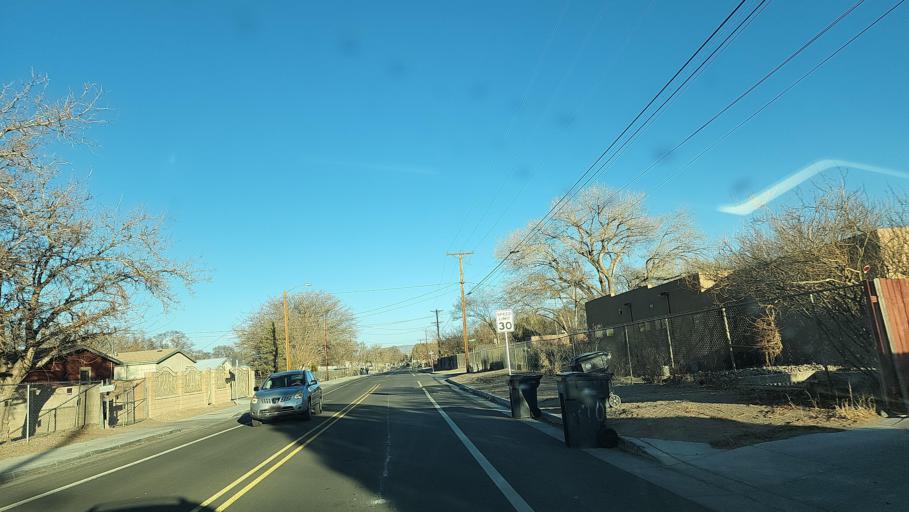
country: US
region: New Mexico
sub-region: Bernalillo County
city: South Valley
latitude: 35.0306
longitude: -106.6989
